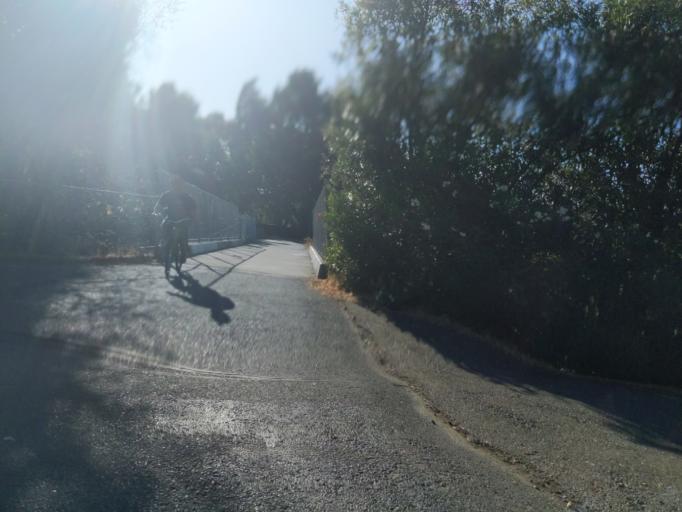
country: US
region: California
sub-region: Contra Costa County
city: Waldon
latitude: 37.9234
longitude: -122.0495
